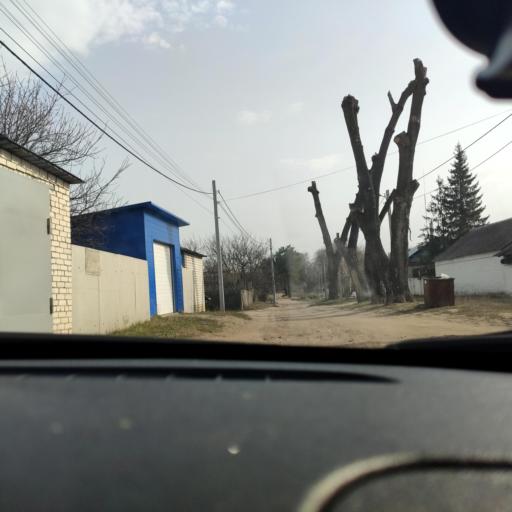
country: RU
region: Voronezj
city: Maslovka
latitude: 51.5643
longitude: 39.2427
